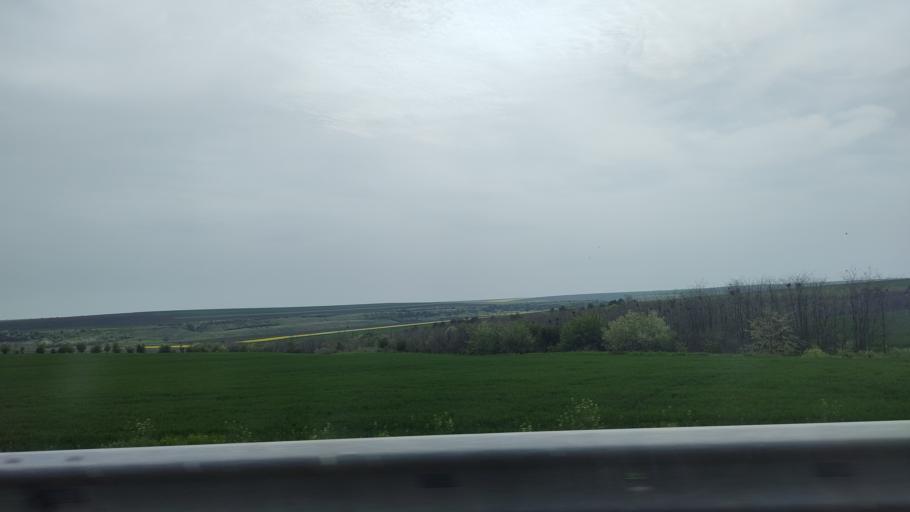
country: RO
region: Constanta
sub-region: Oras Murfatlar
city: Siminoc
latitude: 44.1415
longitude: 28.3554
